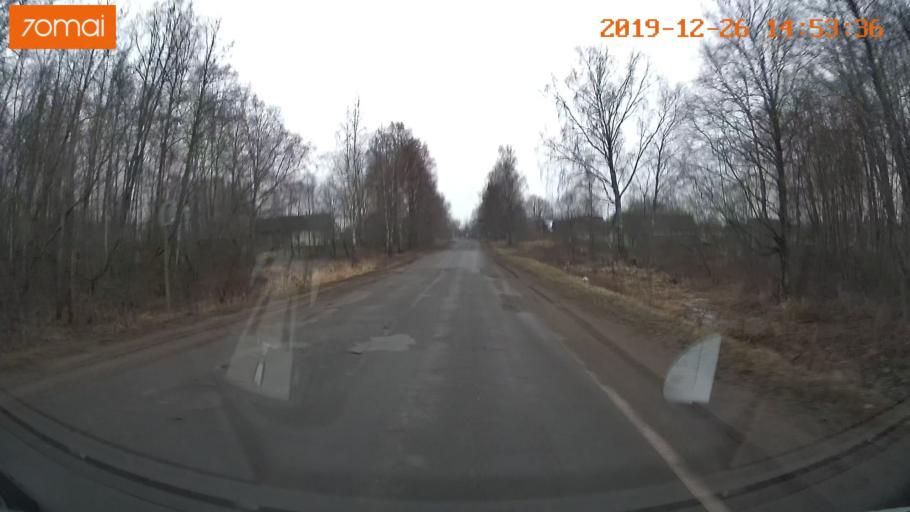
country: RU
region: Jaroslavl
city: Rybinsk
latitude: 58.3138
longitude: 38.8883
